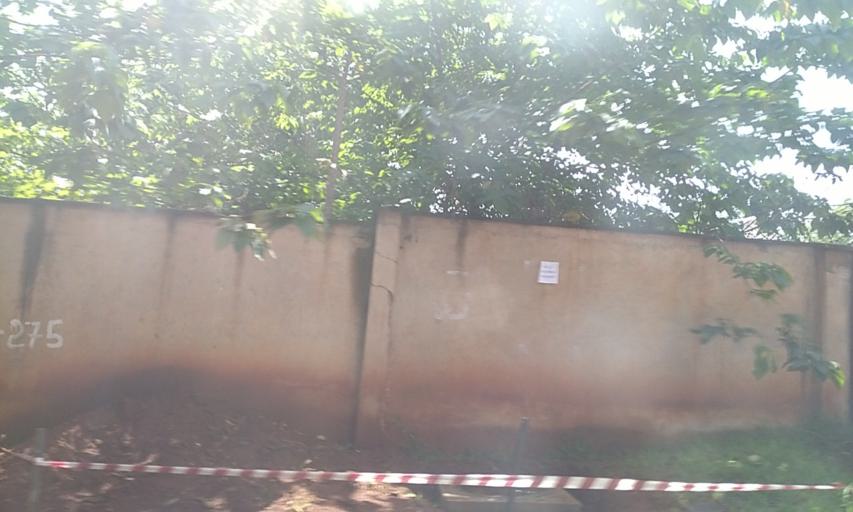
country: UG
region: Central Region
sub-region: Kampala District
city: Kampala
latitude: 0.3284
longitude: 32.6005
